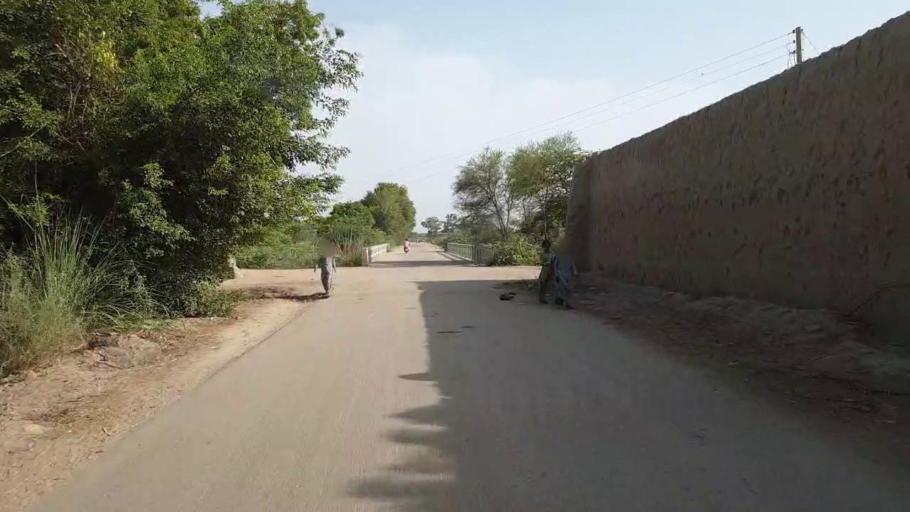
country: PK
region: Sindh
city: Sakrand
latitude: 26.2499
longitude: 68.2846
